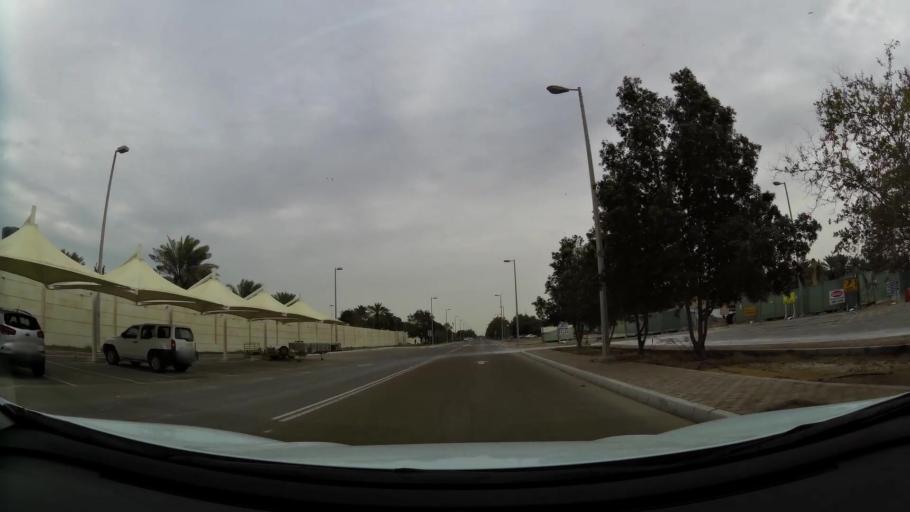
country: AE
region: Abu Dhabi
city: Abu Dhabi
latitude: 24.4130
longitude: 54.4282
